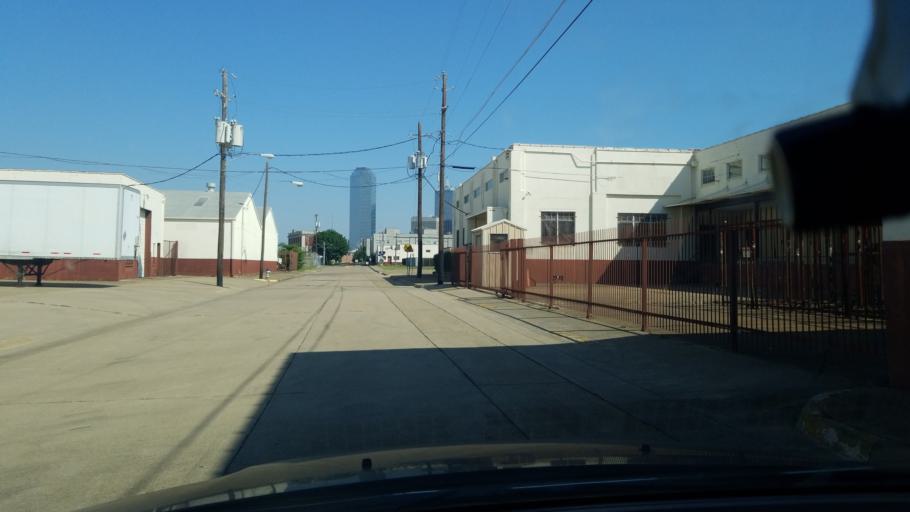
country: US
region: Texas
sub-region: Dallas County
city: Dallas
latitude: 32.7660
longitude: -96.7897
